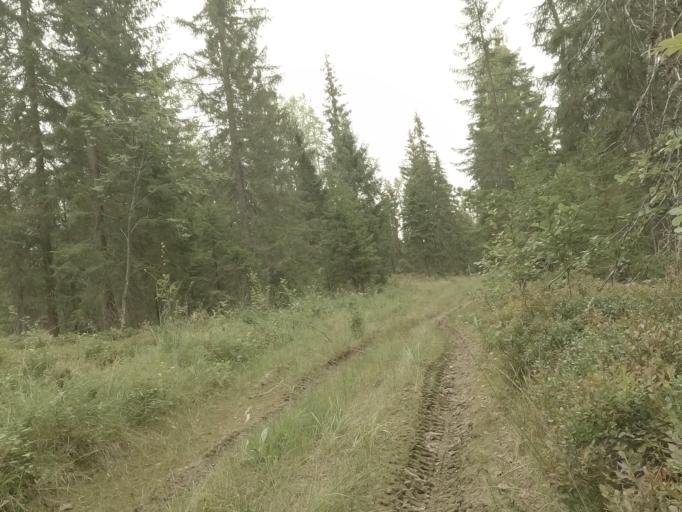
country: RU
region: Leningrad
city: Kamennogorsk
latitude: 61.0507
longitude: 29.1814
